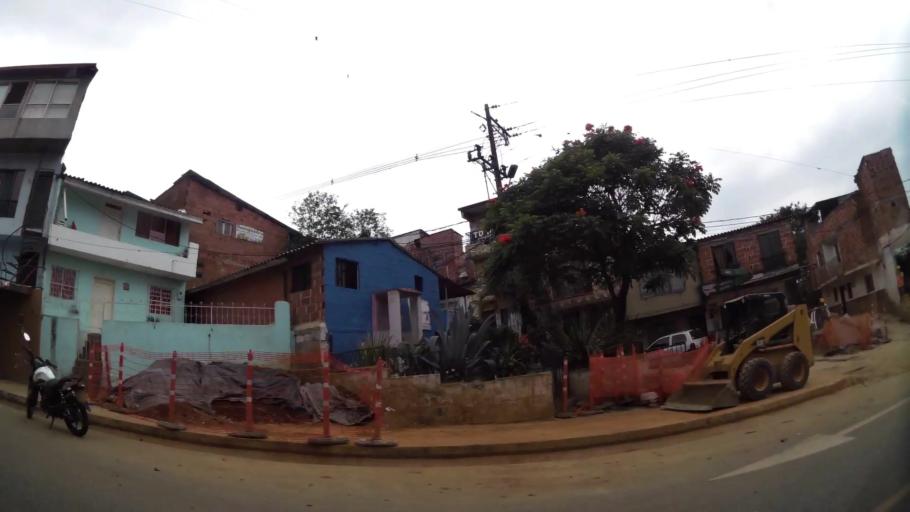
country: CO
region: Antioquia
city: Bello
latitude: 6.2948
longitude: -75.5563
